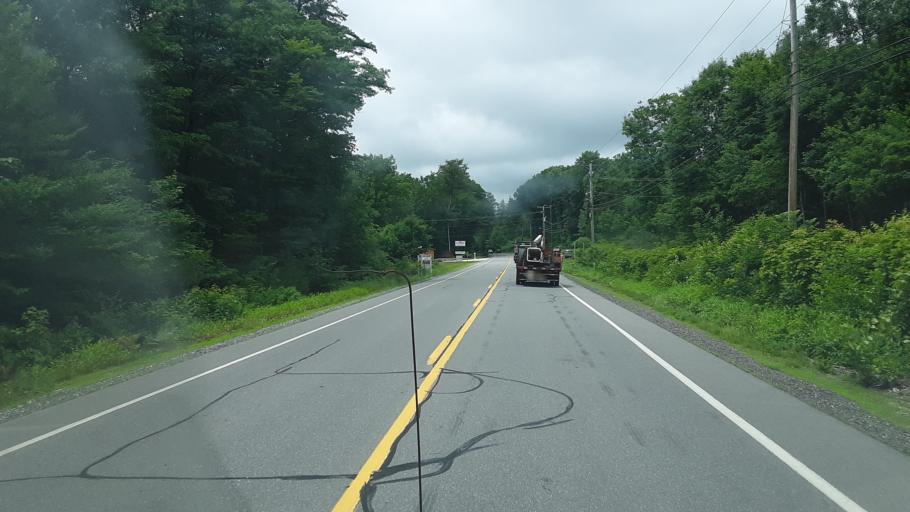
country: US
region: New Hampshire
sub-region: Rockingham County
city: Northwood
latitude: 43.1782
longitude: -71.1034
